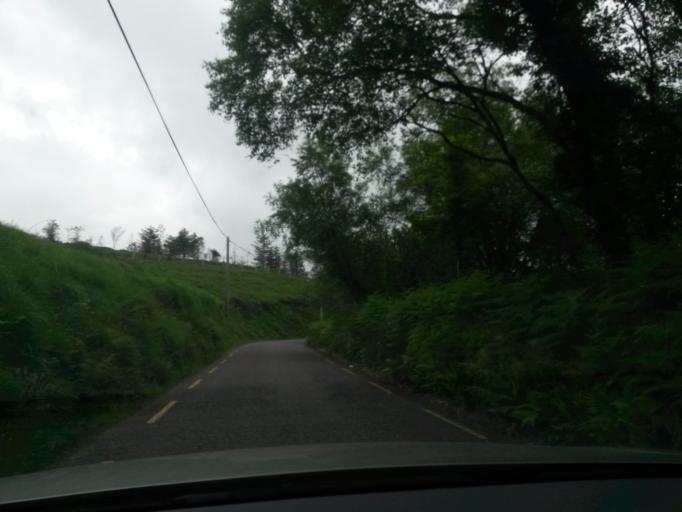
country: IE
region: Munster
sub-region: Ciarrai
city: Killorglin
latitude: 52.0073
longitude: -9.8263
